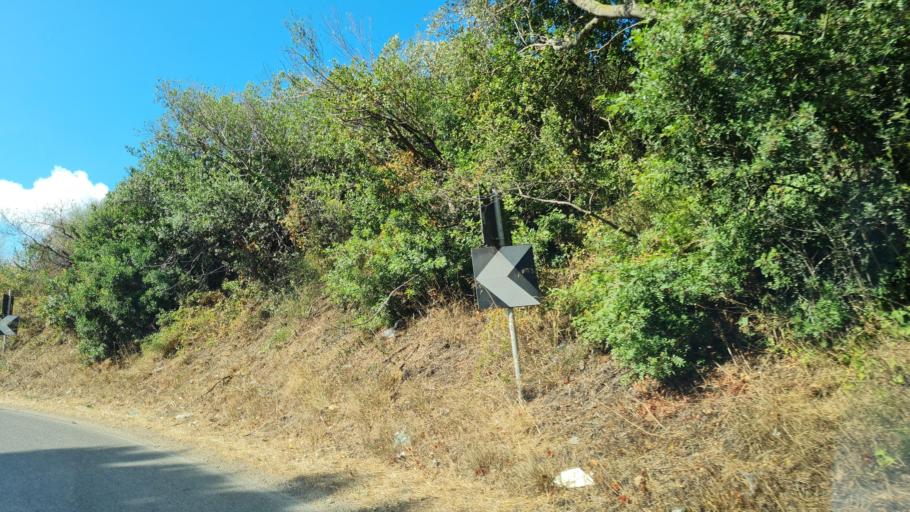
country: IT
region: Latium
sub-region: Provincia di Viterbo
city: Tarquinia
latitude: 42.2538
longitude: 11.7424
